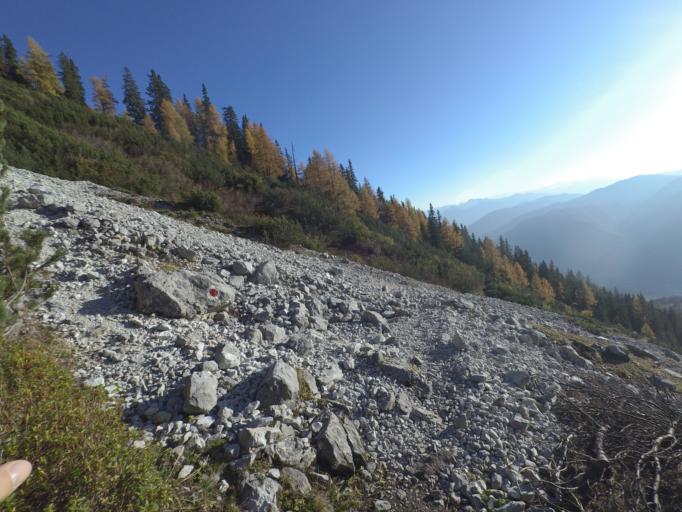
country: AT
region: Salzburg
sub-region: Politischer Bezirk Sankt Johann im Pongau
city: Werfenweng
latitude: 47.4906
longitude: 13.2328
